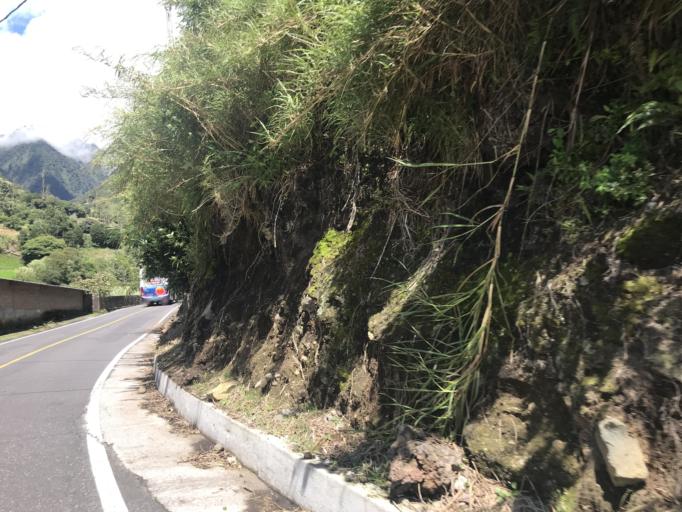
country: EC
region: Tungurahua
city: Banos
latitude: -1.4057
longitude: -78.4056
